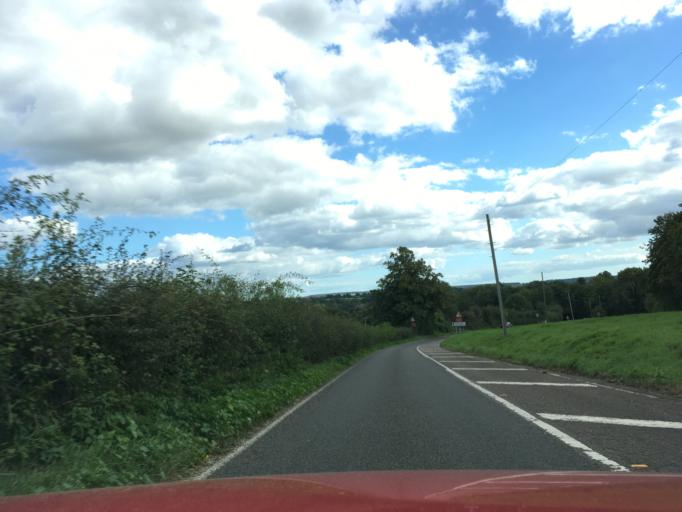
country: GB
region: England
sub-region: Hampshire
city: Abbotts Ann
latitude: 51.1173
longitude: -1.5021
